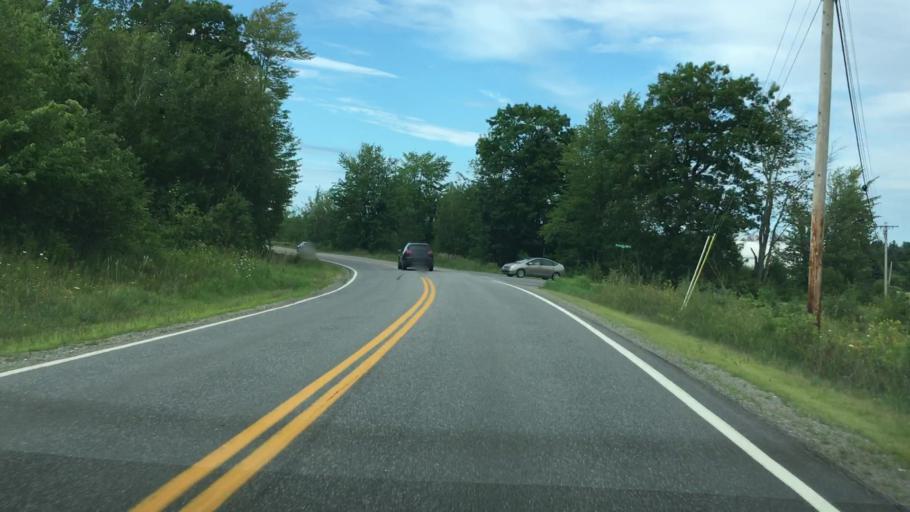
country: US
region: Maine
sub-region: Waldo County
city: Belfast
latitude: 44.3736
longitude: -69.0321
